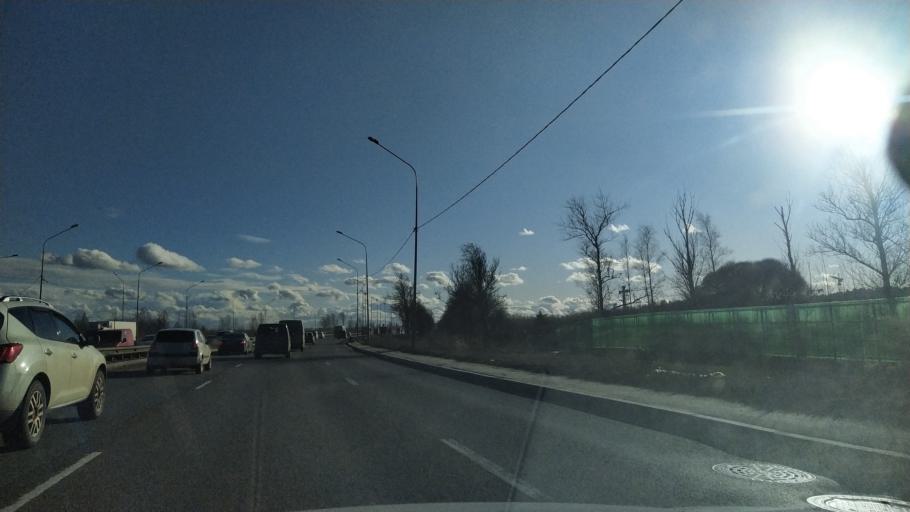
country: RU
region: St.-Petersburg
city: Aleksandrovskaya
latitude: 59.7644
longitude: 30.3297
